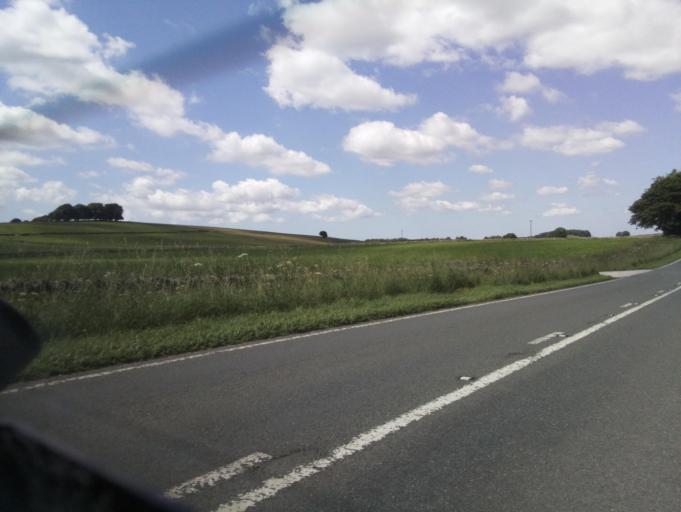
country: GB
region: England
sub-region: Derbyshire
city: Bakewell
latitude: 53.1428
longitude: -1.7583
